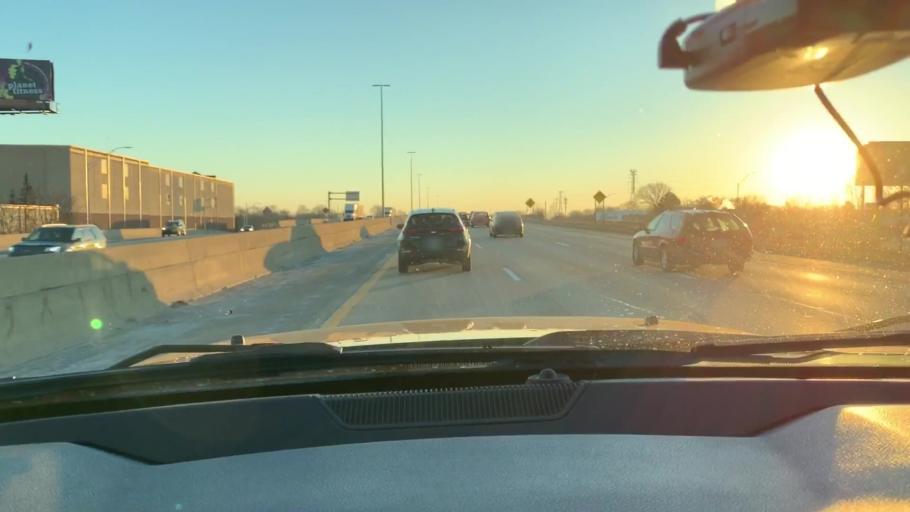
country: US
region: Michigan
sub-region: Wayne County
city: Lincoln Park
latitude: 42.2550
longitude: -83.1834
